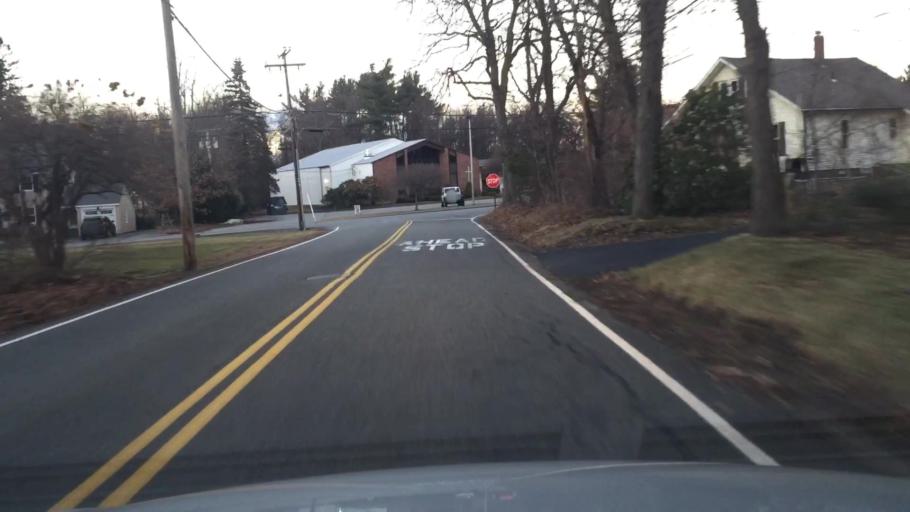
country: US
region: Massachusetts
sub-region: Worcester County
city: West Boylston
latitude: 42.3333
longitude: -71.8190
